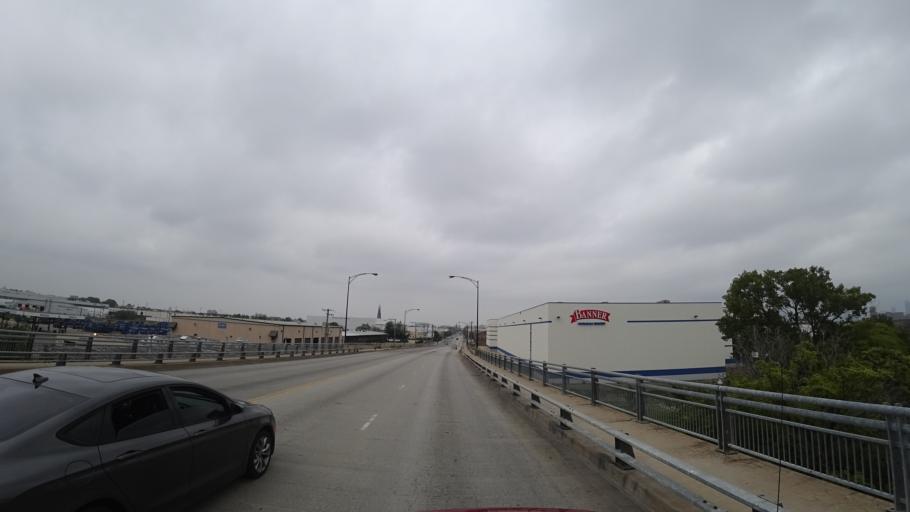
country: US
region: Illinois
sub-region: Cook County
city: Chicago
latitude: 41.8419
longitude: -87.6755
